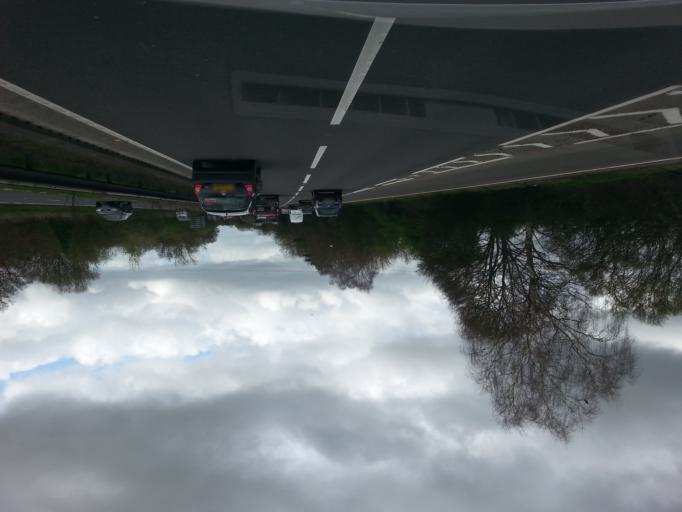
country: GB
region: England
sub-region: Hampshire
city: Andover
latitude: 51.1866
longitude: -1.4068
